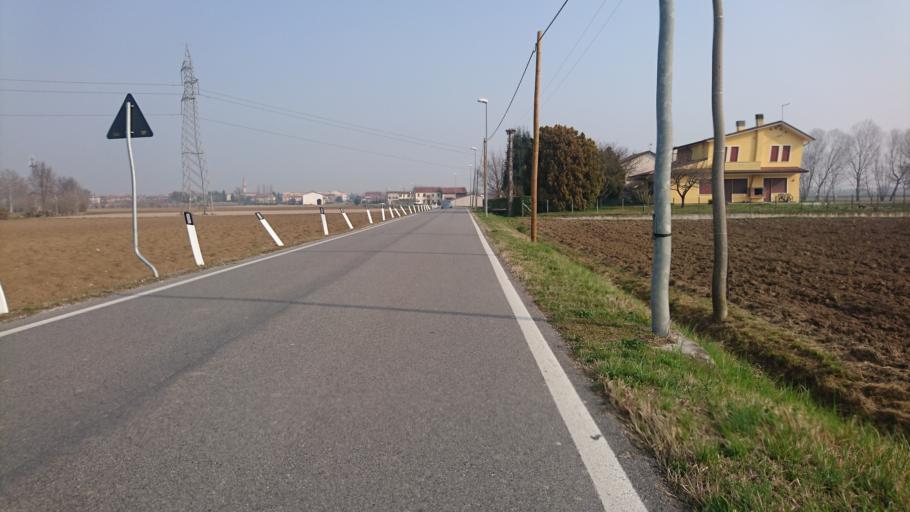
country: IT
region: Veneto
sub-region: Provincia di Padova
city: Veggiano
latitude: 45.4398
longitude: 11.7147
